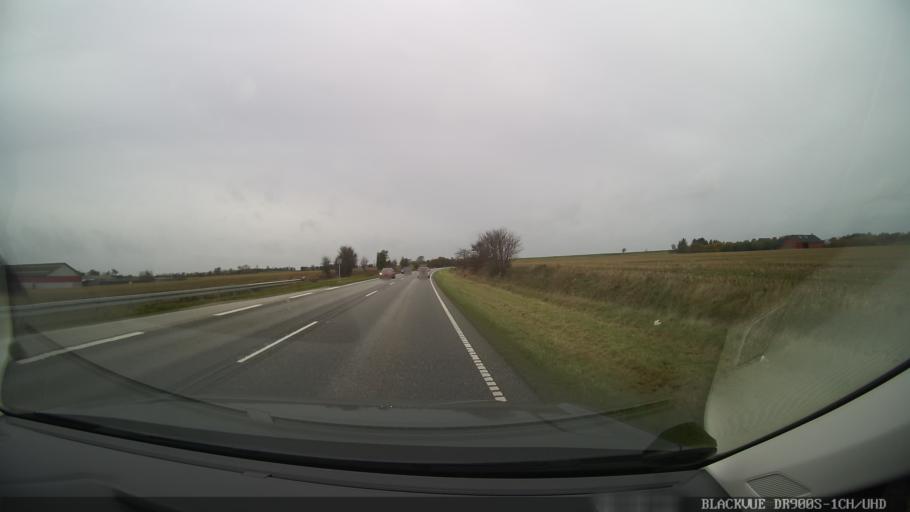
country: DK
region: North Denmark
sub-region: Morso Kommune
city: Nykobing Mors
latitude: 56.8259
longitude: 8.7326
